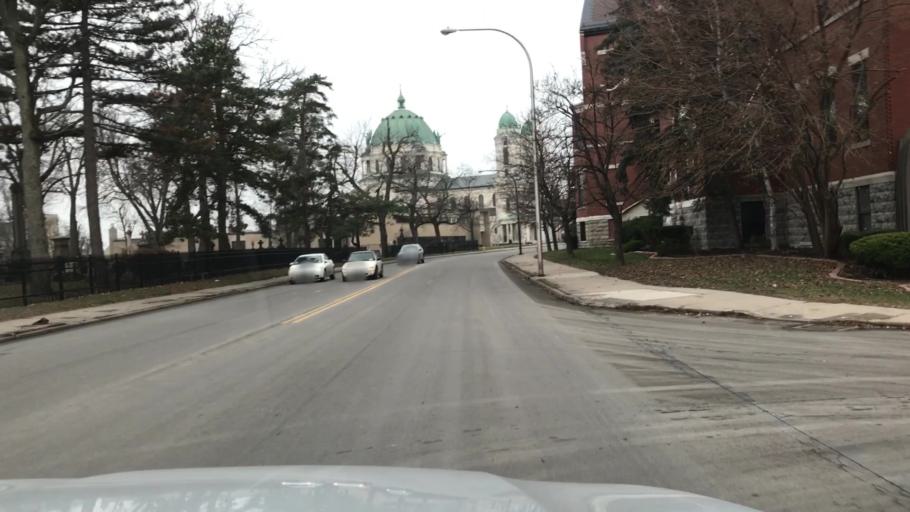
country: US
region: New York
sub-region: Erie County
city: Lackawanna
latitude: 42.8262
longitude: -78.8208
